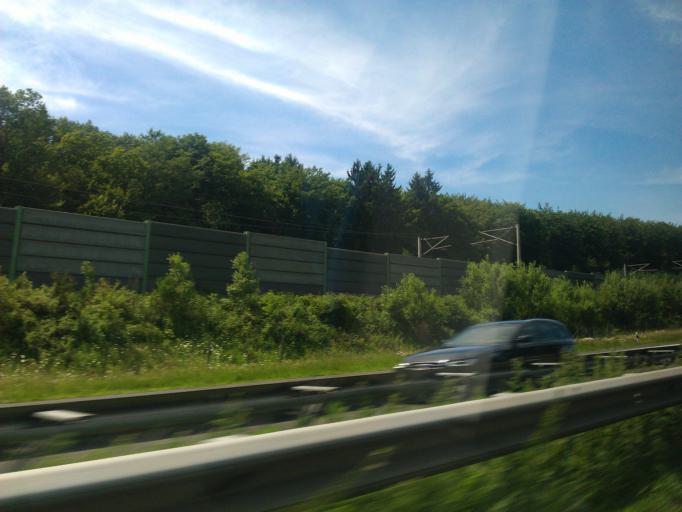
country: DE
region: Rheinland-Pfalz
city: Dernbach
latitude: 50.5402
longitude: 7.5916
